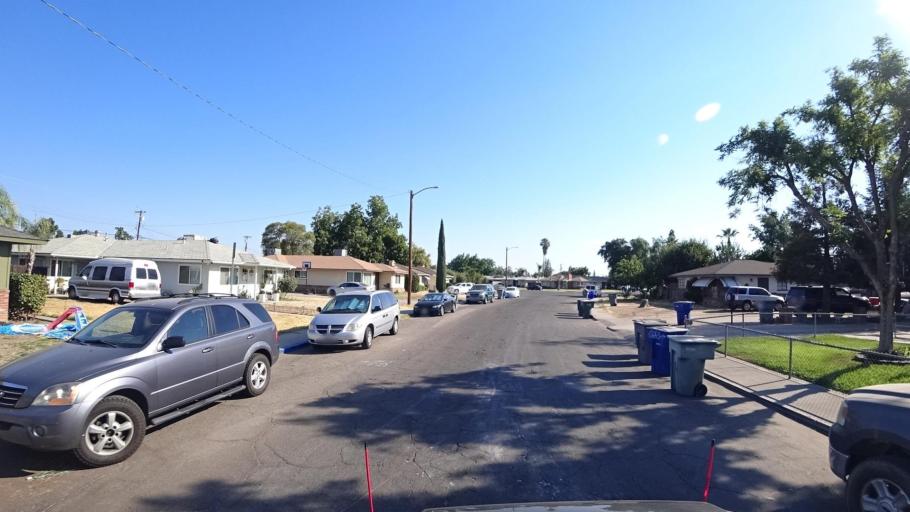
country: US
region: California
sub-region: Fresno County
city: Fresno
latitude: 36.7730
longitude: -119.7713
